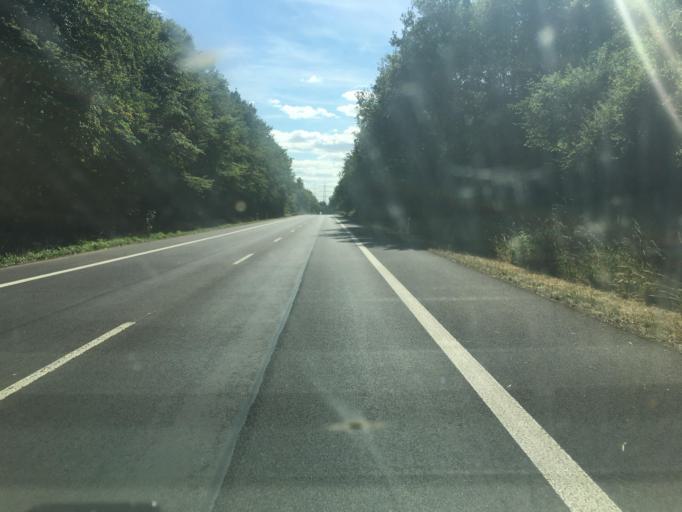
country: DE
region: North Rhine-Westphalia
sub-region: Regierungsbezirk Koln
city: Bergheim
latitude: 50.9633
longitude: 6.6242
